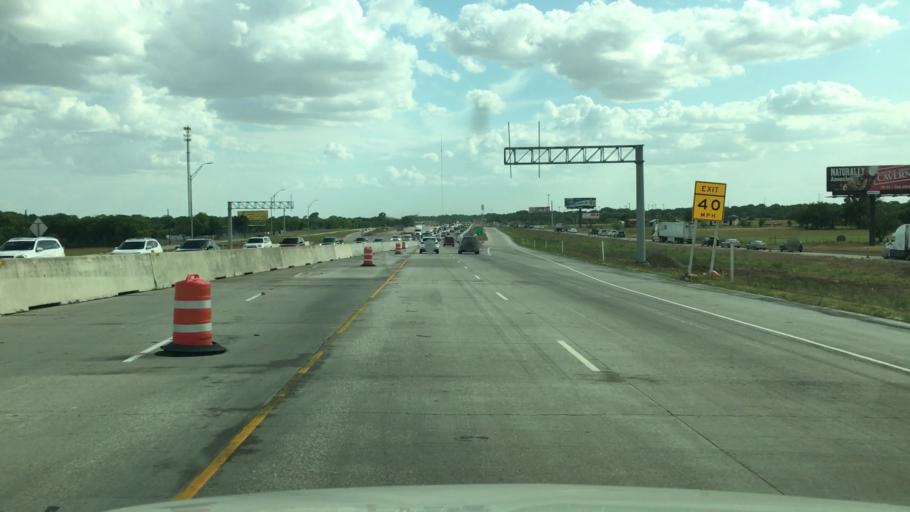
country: US
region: Texas
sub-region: McLennan County
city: Bruceville-Eddy
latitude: 31.3059
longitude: -97.2457
